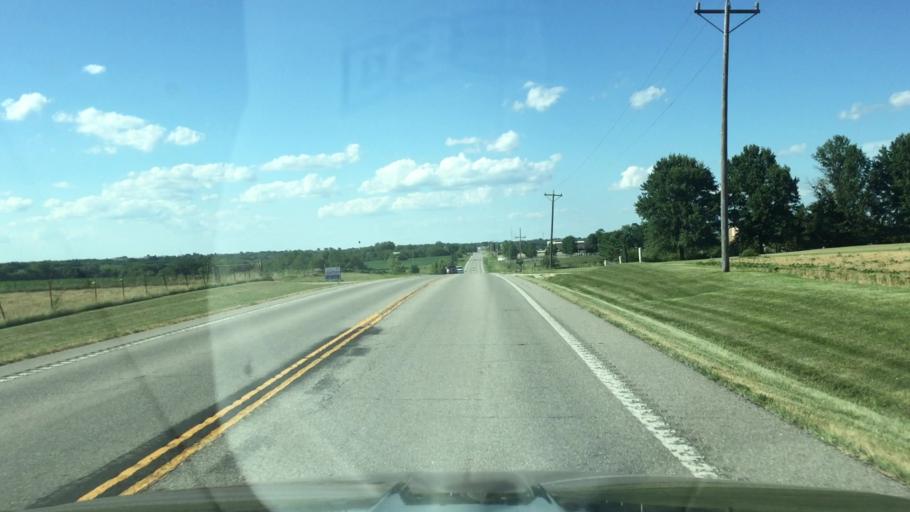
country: US
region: Missouri
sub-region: Moniteau County
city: Tipton
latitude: 38.6133
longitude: -92.7901
